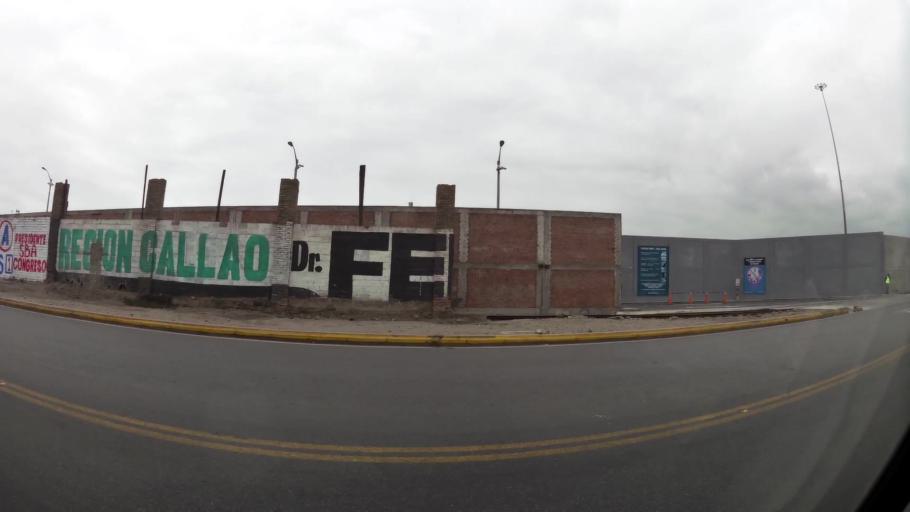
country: PE
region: Callao
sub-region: Callao
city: Callao
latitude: -12.0482
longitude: -77.1368
